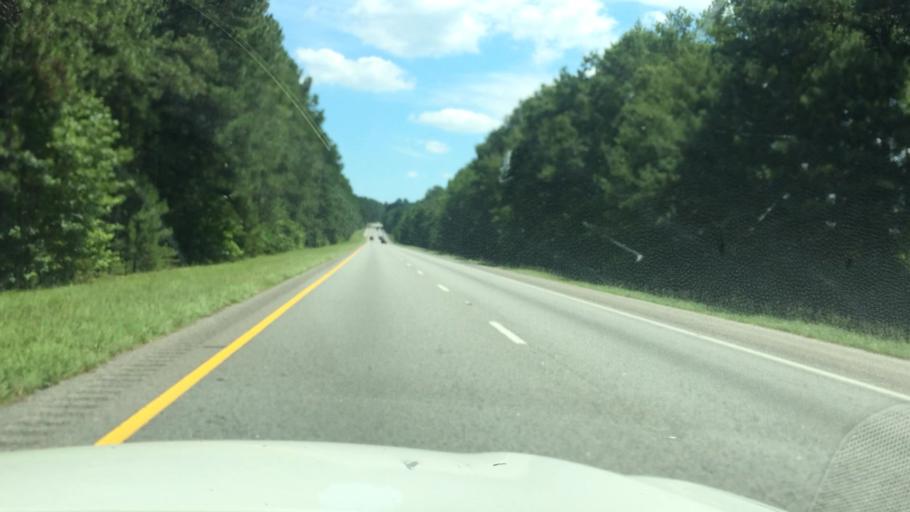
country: US
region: South Carolina
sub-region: Aiken County
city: Aiken
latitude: 33.6950
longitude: -81.6101
